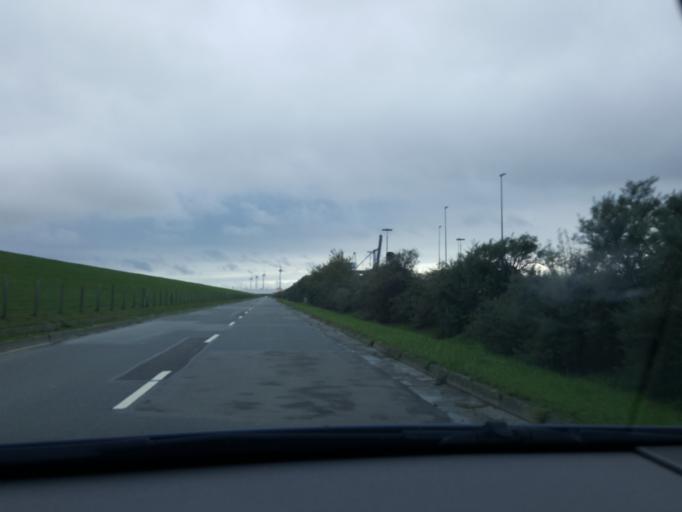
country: DE
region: Lower Saxony
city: Emden
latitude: 53.3335
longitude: 7.2122
